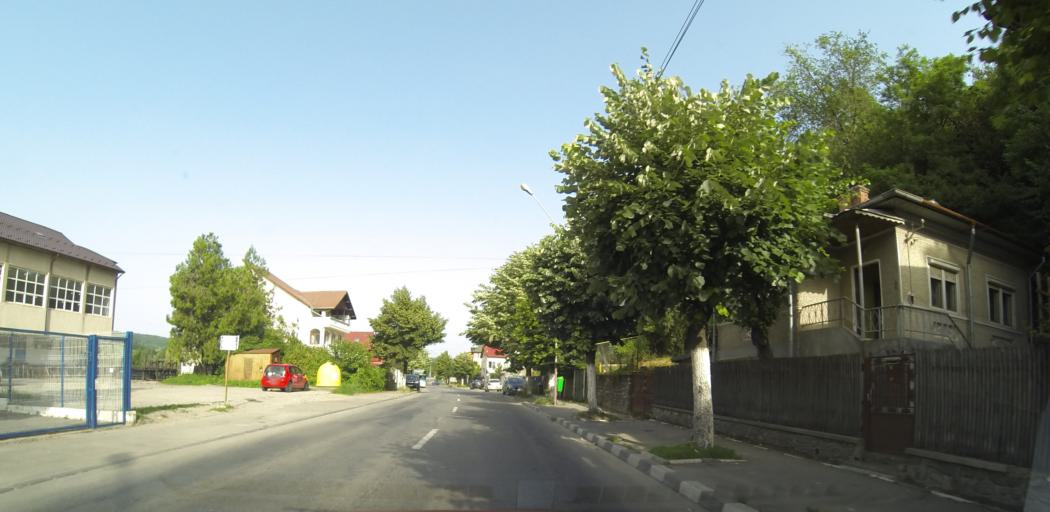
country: RO
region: Valcea
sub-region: Municipiul Ramnicu Valcea
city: Ramnicu Valcea
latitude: 45.1057
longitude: 24.3470
